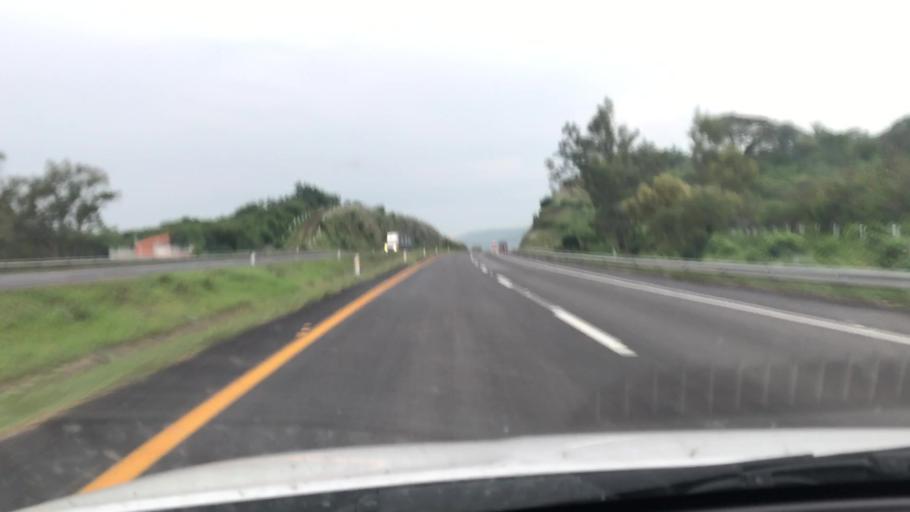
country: MX
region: Jalisco
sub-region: Zapotlanejo
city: La Mezquitera
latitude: 20.5309
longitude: -103.0105
